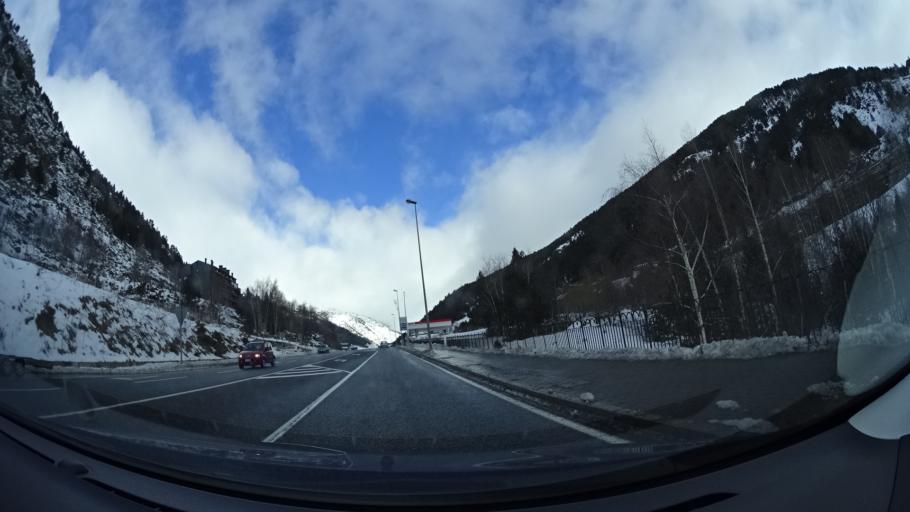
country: AD
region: Canillo
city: El Tarter
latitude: 42.5806
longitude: 1.6604
